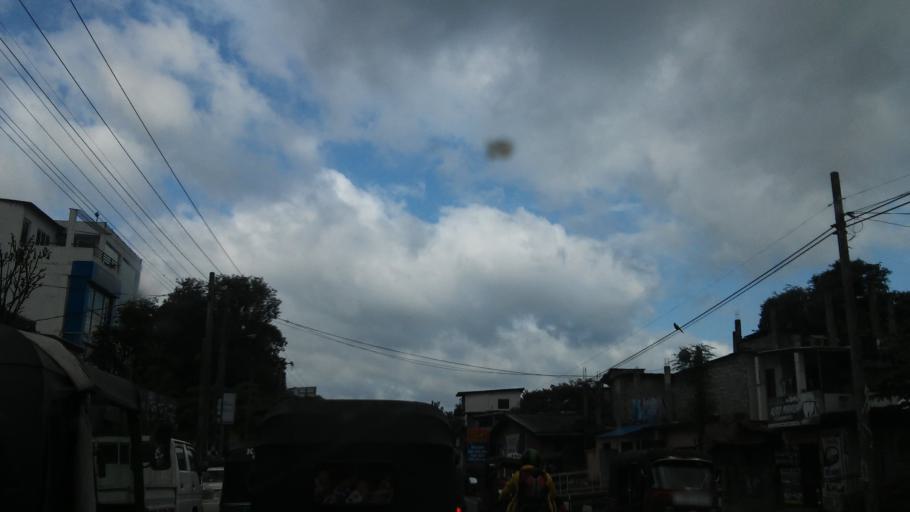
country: LK
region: Central
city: Kandy
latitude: 7.2856
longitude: 80.6281
